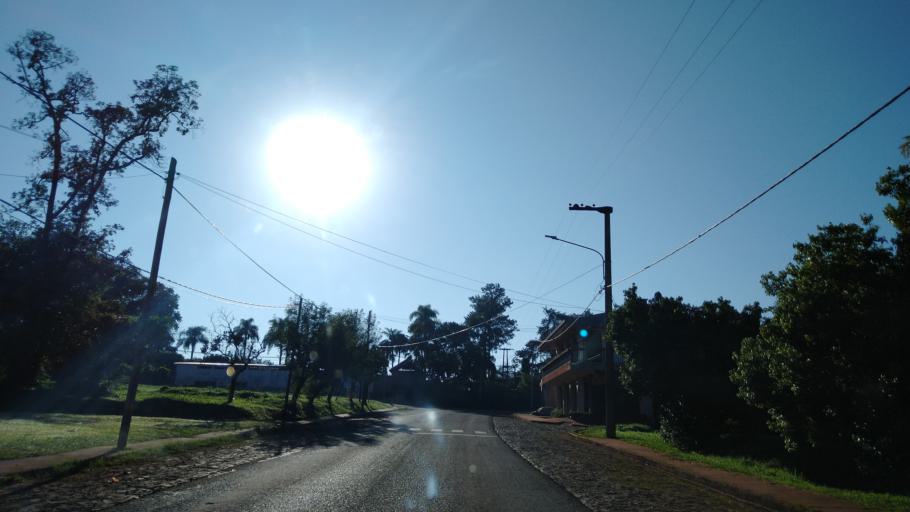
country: AR
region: Misiones
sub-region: Departamento de Montecarlo
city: Montecarlo
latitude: -26.5718
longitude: -54.7515
